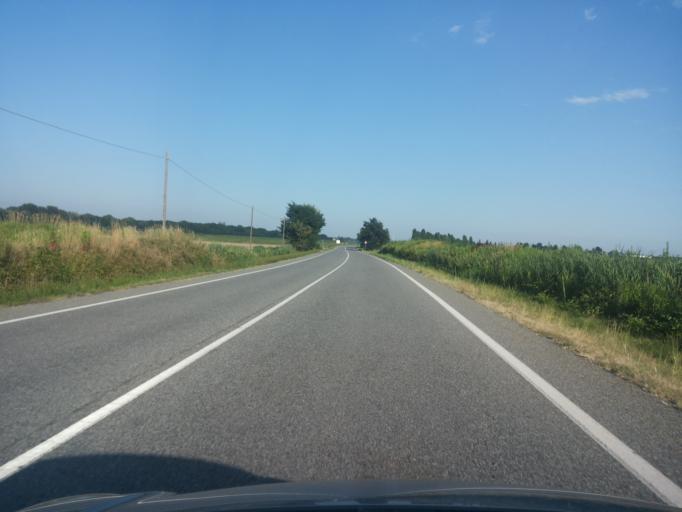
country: IT
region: Piedmont
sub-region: Provincia di Vercelli
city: Casanova Elvo
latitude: 45.4157
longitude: 8.3147
